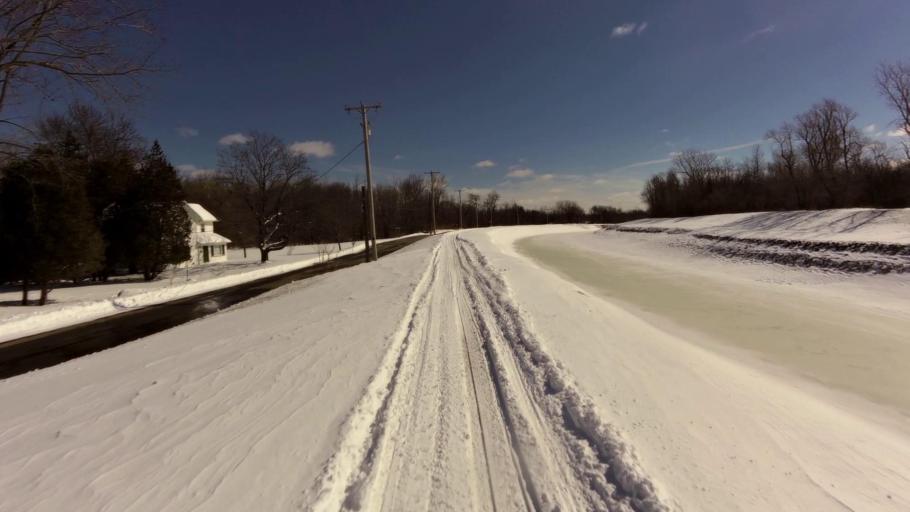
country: US
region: New York
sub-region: Orleans County
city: Holley
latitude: 43.2544
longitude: -78.0820
